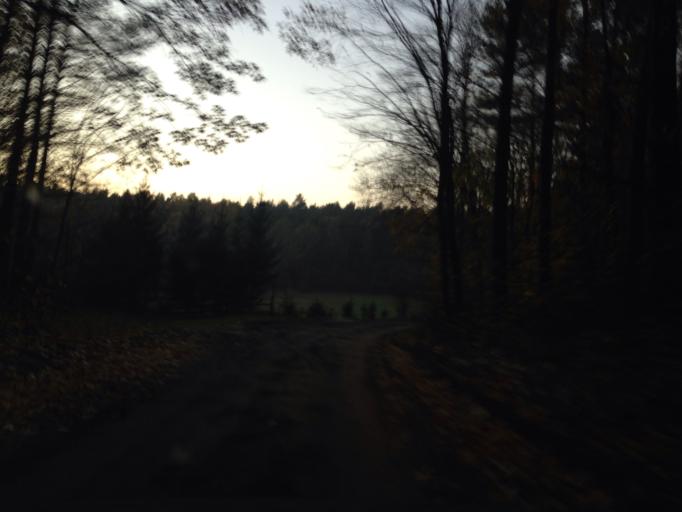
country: PL
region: Kujawsko-Pomorskie
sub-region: Powiat brodnicki
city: Gorzno
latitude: 53.2259
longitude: 19.7192
